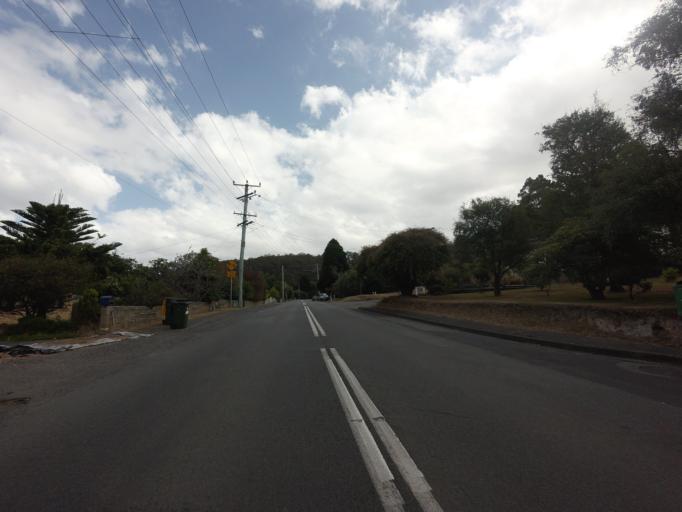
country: AU
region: Tasmania
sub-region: Hobart
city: Dynnyrne
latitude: -42.9132
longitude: 147.2688
